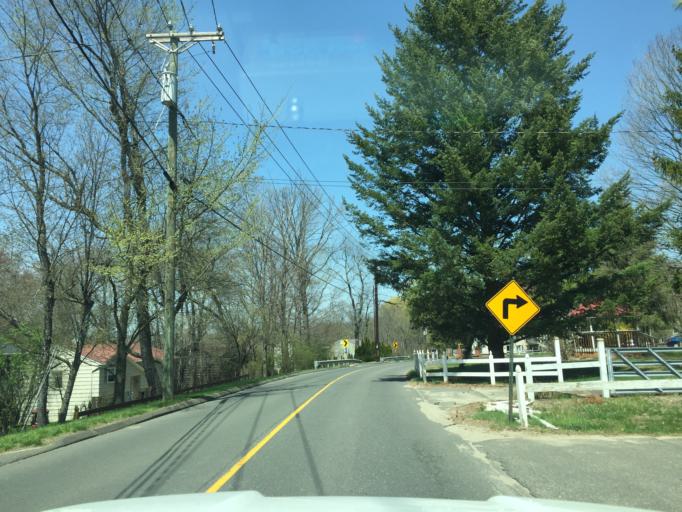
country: US
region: Connecticut
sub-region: Fairfield County
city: Bethel
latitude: 41.3981
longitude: -73.4040
